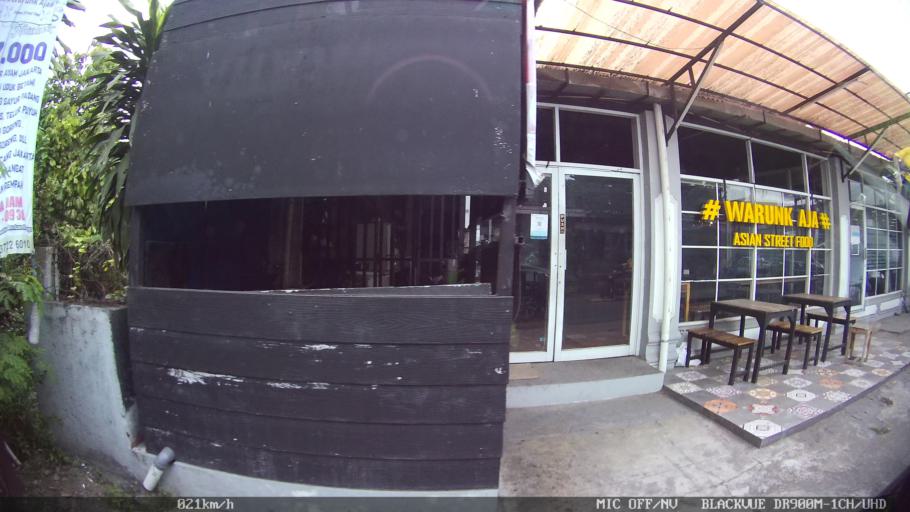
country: ID
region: Daerah Istimewa Yogyakarta
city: Yogyakarta
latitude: -7.7901
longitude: 110.3984
